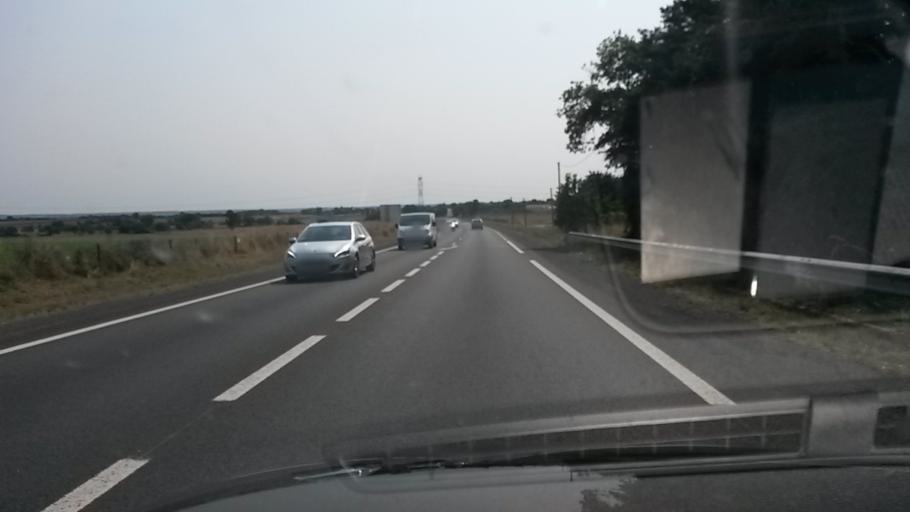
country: FR
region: Pays de la Loire
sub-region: Departement de la Loire-Atlantique
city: Mesanger
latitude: 47.4300
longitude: -1.1862
